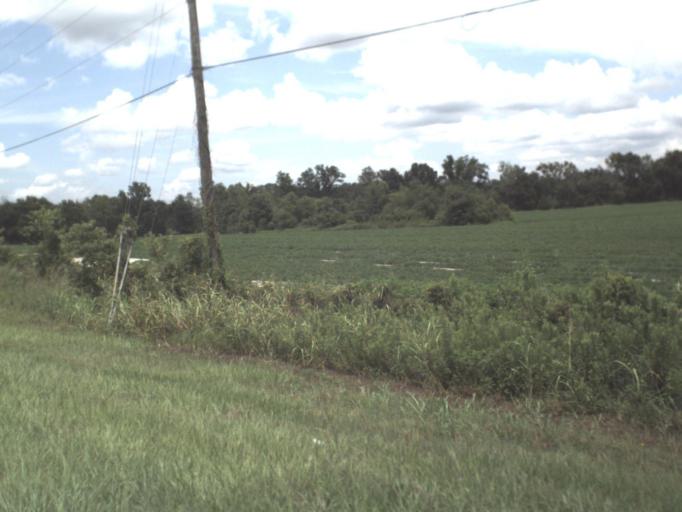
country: US
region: Florida
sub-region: Madison County
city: Madison
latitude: 30.5558
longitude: -83.3671
